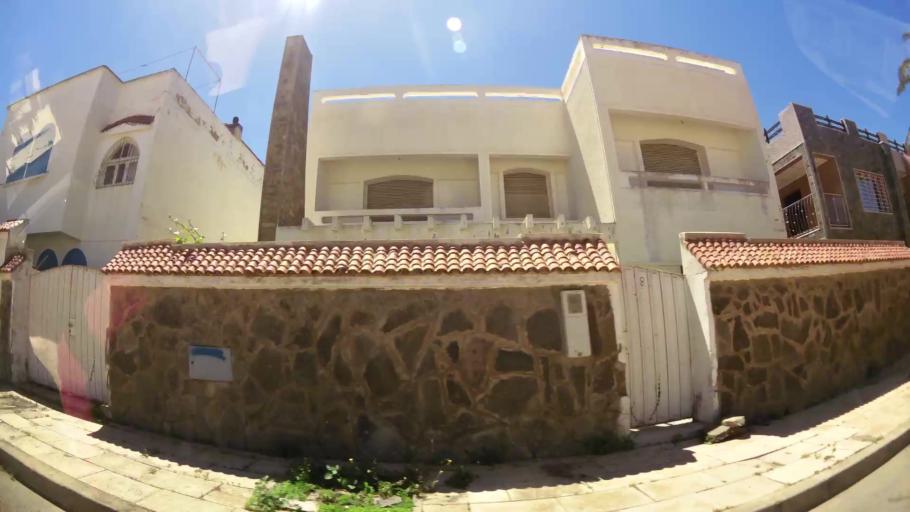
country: MA
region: Oriental
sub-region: Berkane-Taourirt
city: Madagh
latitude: 35.0862
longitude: -2.2309
